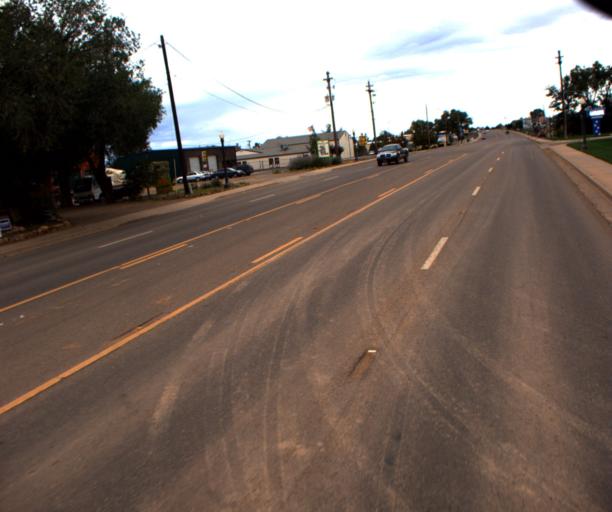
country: US
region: Arizona
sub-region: Navajo County
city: Snowflake
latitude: 34.5018
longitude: -110.0791
